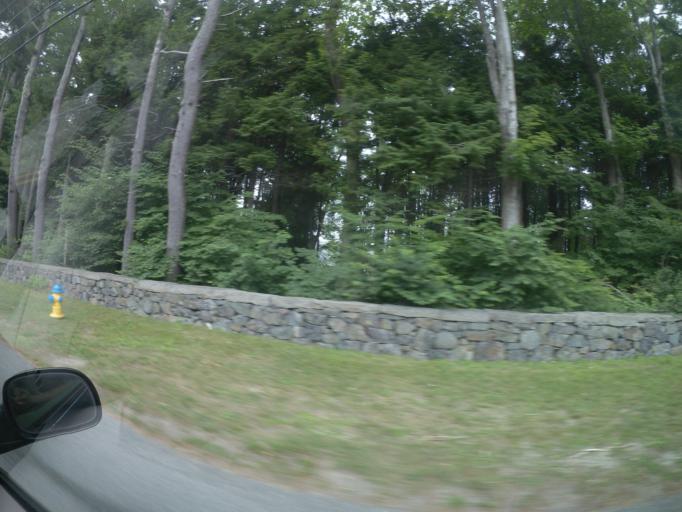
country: US
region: Maine
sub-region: York County
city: Kennebunkport
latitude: 43.3553
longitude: -70.4791
